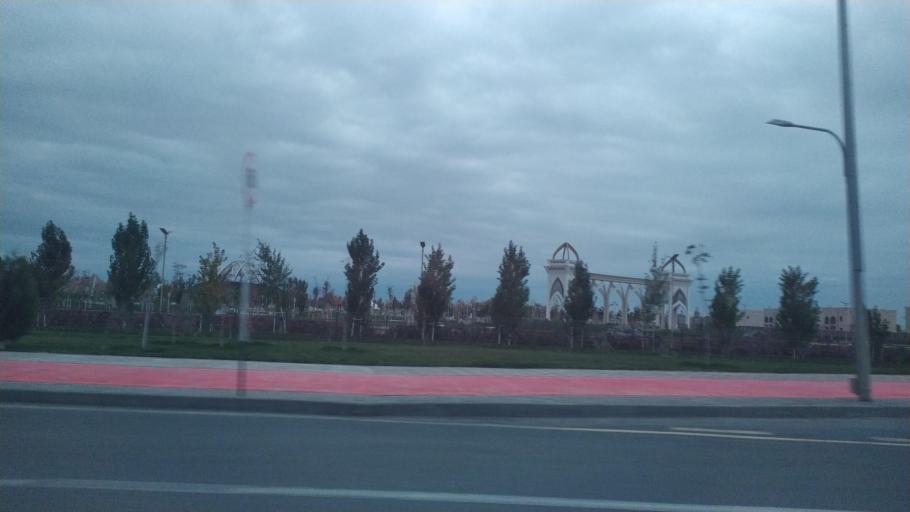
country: KZ
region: Ongtustik Qazaqstan
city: Turkestan
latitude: 43.2765
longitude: 68.3321
